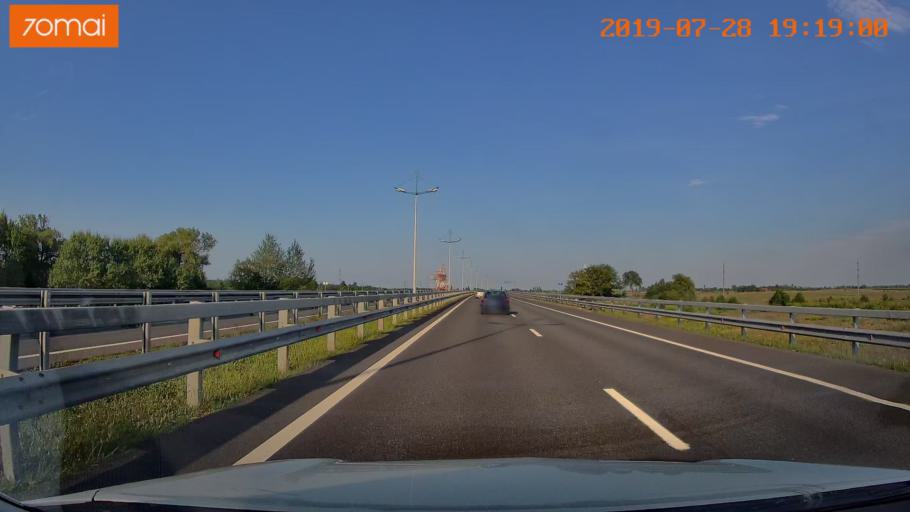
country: RU
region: Kaliningrad
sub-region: Zelenogradskiy Rayon
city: Zelenogradsk
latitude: 54.9205
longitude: 20.4476
